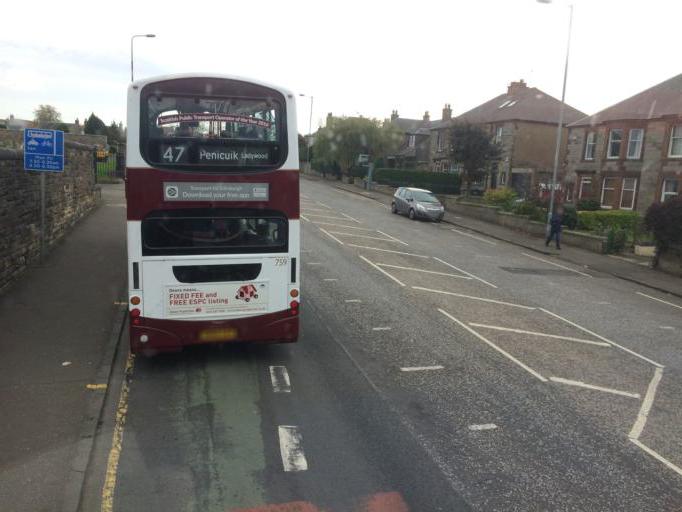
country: GB
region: Scotland
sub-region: Midlothian
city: Loanhead
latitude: 55.9143
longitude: -3.1648
